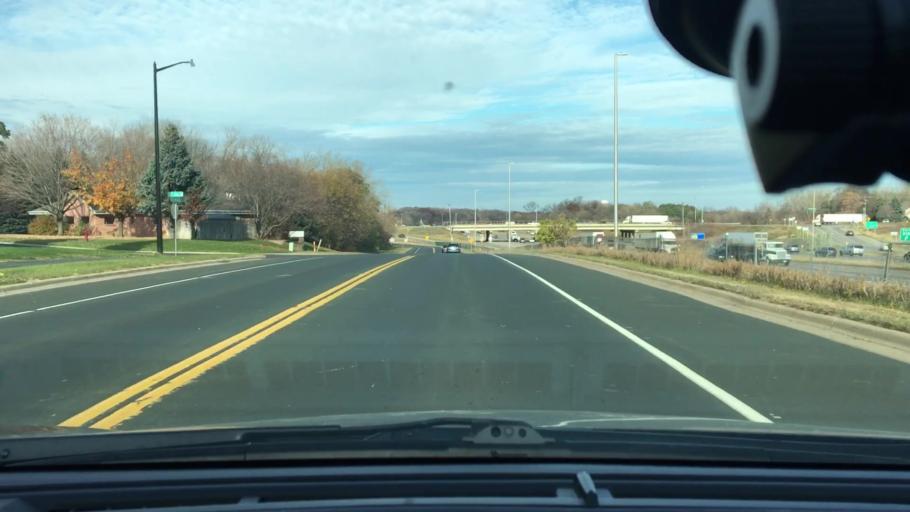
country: US
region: Minnesota
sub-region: Hennepin County
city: Maple Grove
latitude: 45.1017
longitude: -93.4573
